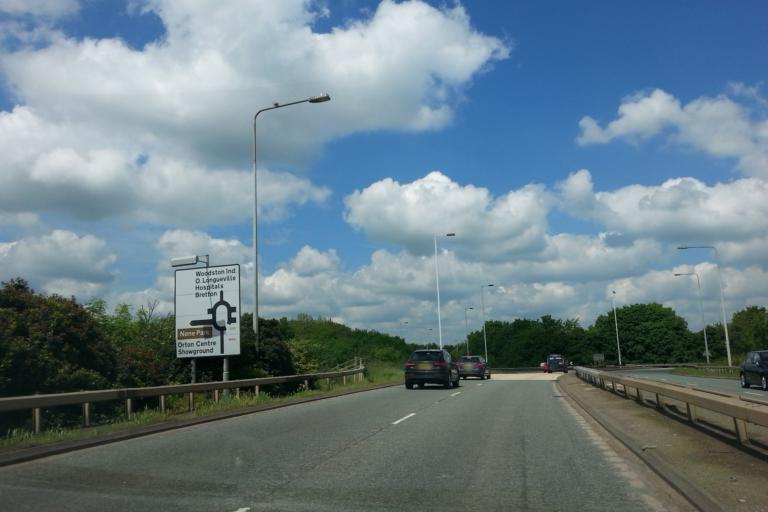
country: GB
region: England
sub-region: Cambridgeshire
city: Yaxley
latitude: 52.5441
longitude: -0.2636
